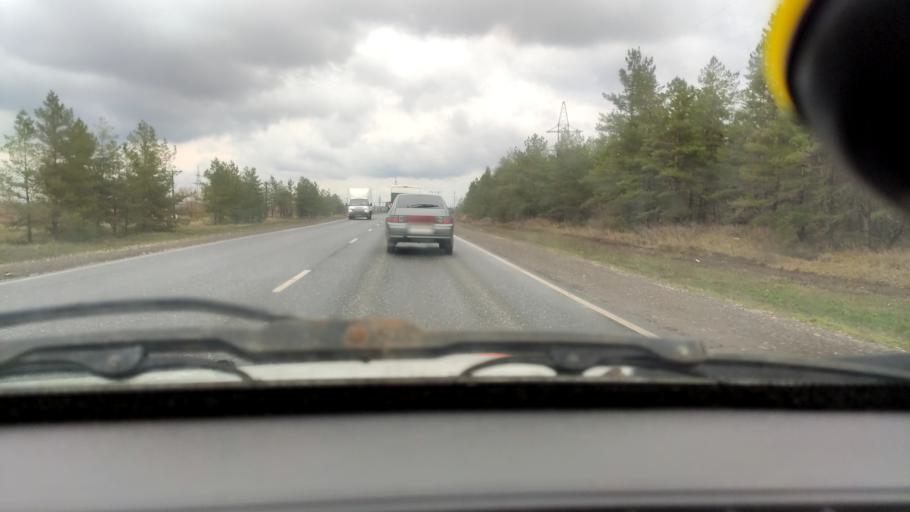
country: RU
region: Samara
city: Zhigulevsk
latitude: 53.5697
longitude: 49.5504
